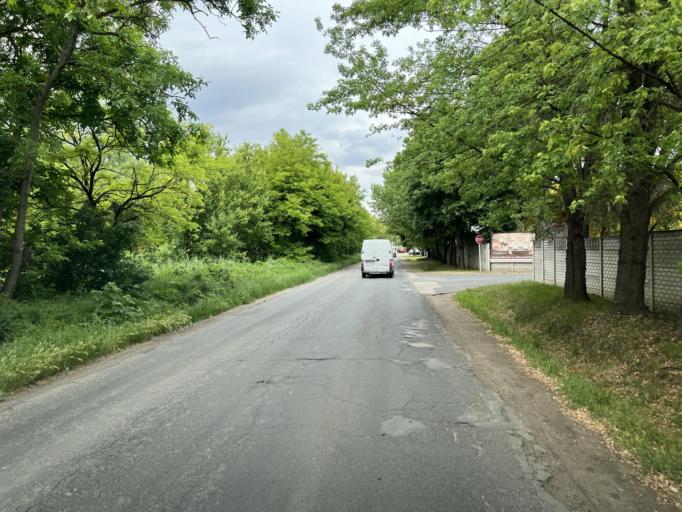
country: HU
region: Pest
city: Nagytarcsa
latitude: 47.5358
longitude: 19.2784
